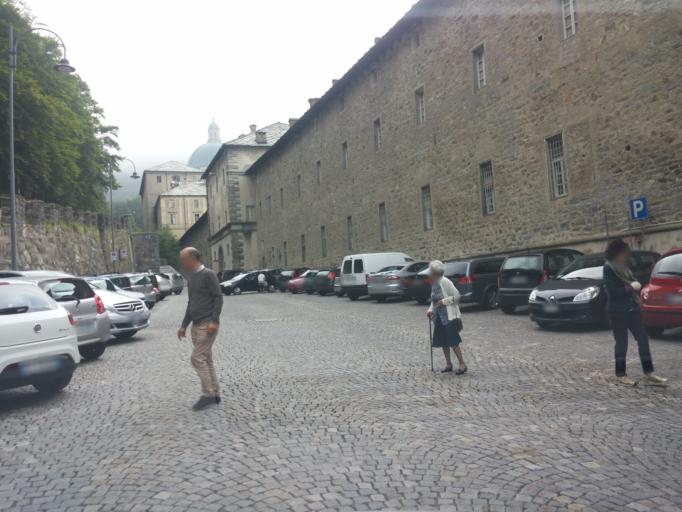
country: IT
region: Piedmont
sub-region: Provincia di Biella
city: San Paolo Cervo
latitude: 45.6264
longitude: 7.9807
